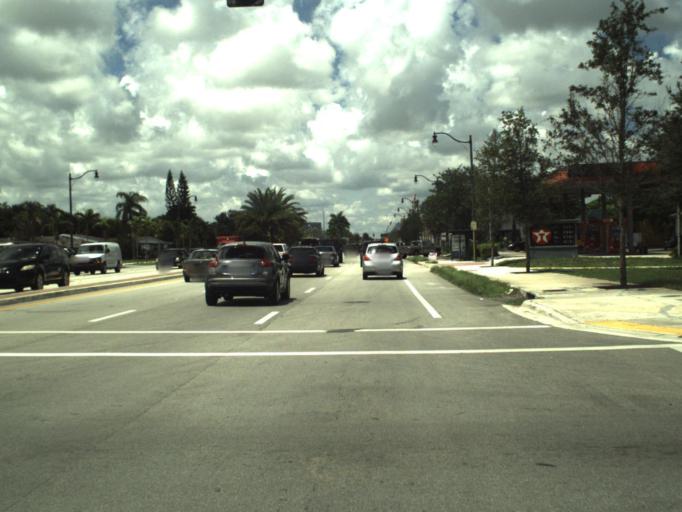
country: US
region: Florida
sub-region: Broward County
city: Carver Ranches
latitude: 26.0103
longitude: -80.1995
